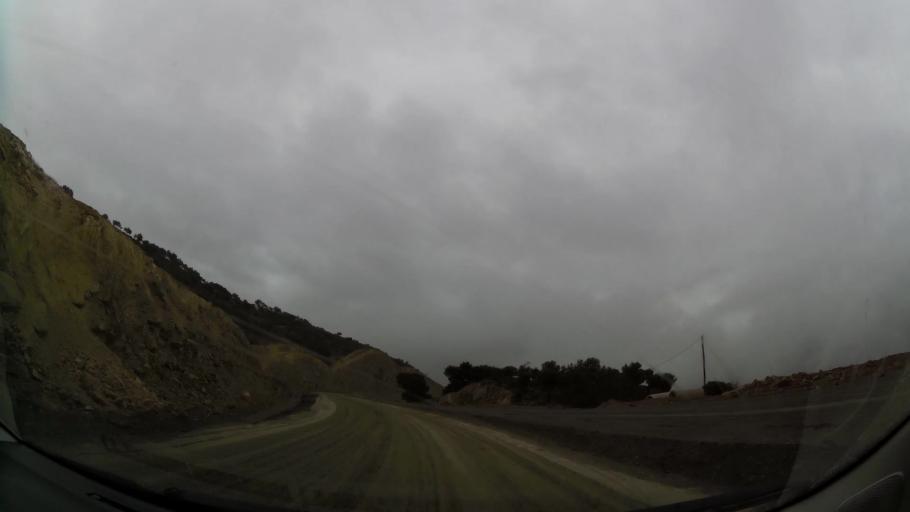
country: MA
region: Taza-Al Hoceima-Taounate
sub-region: Taza
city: Ajdir
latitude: 34.9000
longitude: -3.7857
